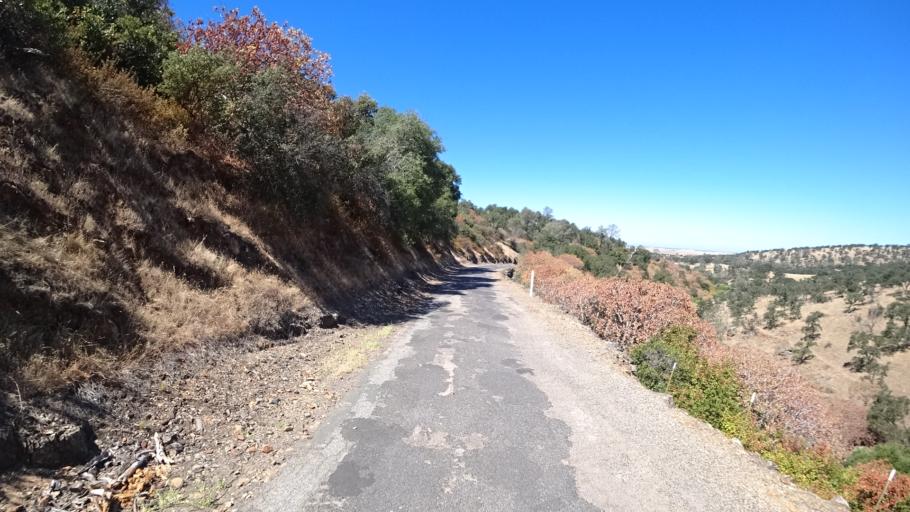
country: US
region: California
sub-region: Calaveras County
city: Rancho Calaveras
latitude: 38.0213
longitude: -120.7795
